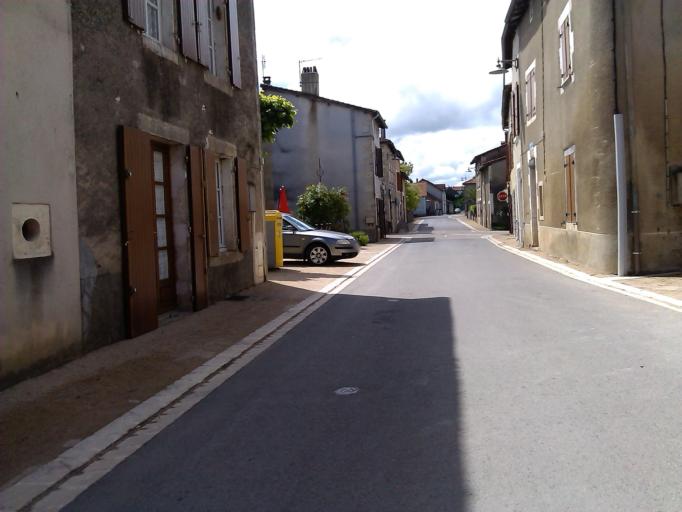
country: FR
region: Poitou-Charentes
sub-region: Departement de la Charente
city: Champagne-Mouton
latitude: 46.0383
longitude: 0.4522
